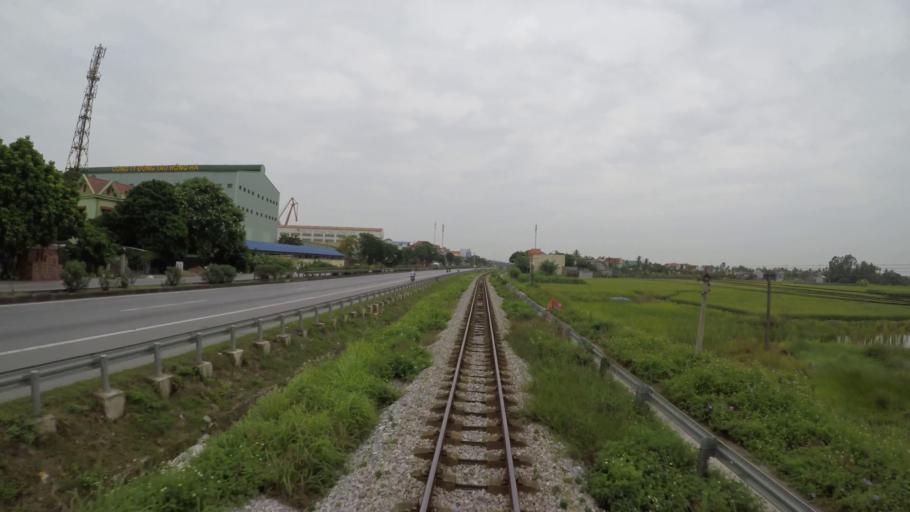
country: VN
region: Hai Duong
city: Phu Thai
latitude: 20.9433
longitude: 106.5438
